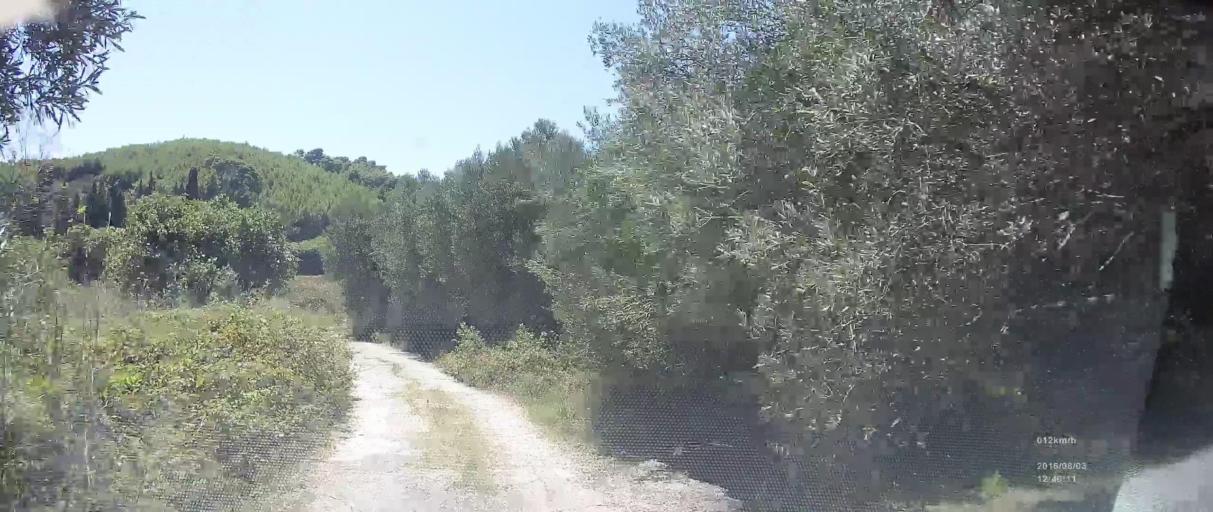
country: HR
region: Dubrovacko-Neretvanska
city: Blato
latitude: 42.7306
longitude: 17.5567
